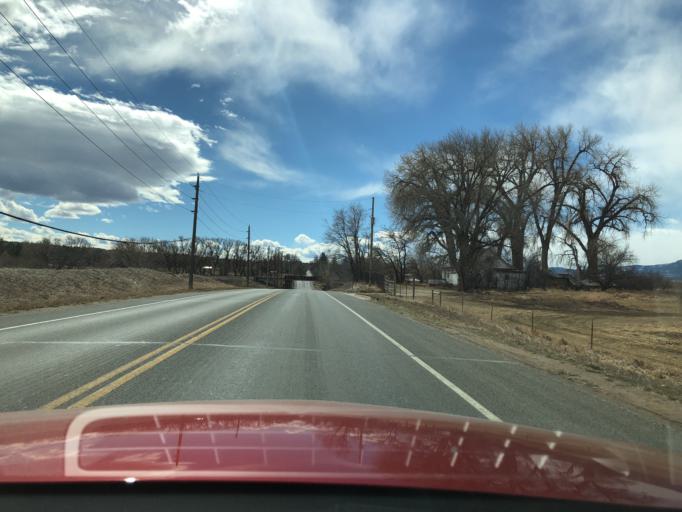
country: US
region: Colorado
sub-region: Boulder County
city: Gunbarrel
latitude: 40.0117
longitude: -105.1781
